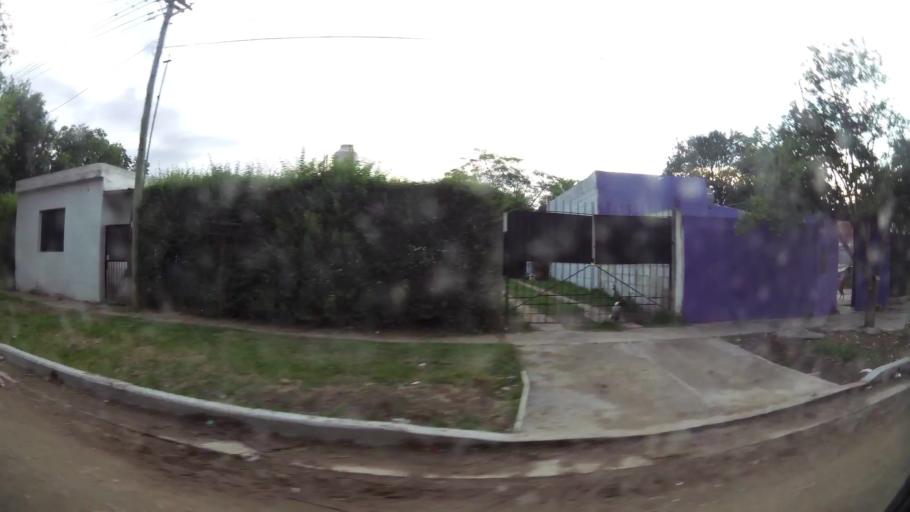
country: AR
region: Buenos Aires
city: San Nicolas de los Arroyos
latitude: -33.3164
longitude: -60.2405
